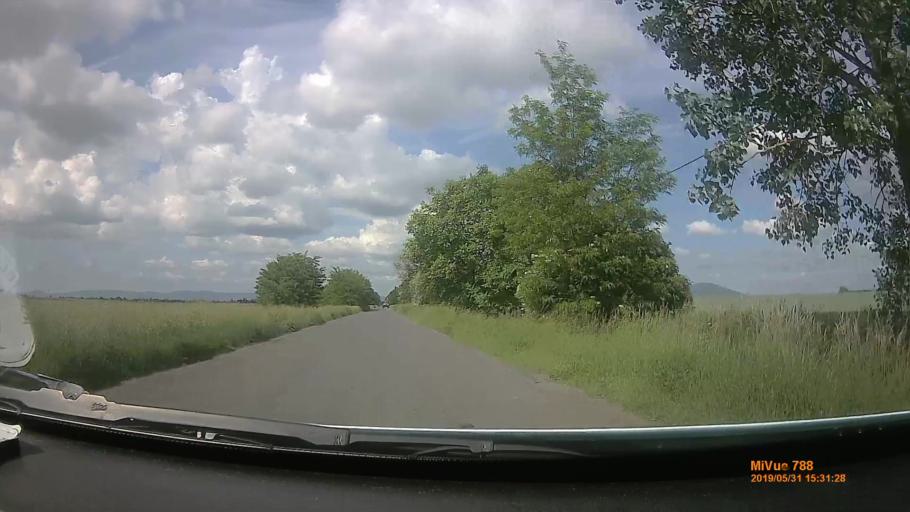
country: HU
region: Borsod-Abauj-Zemplen
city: Prugy
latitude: 48.0624
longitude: 21.2314
